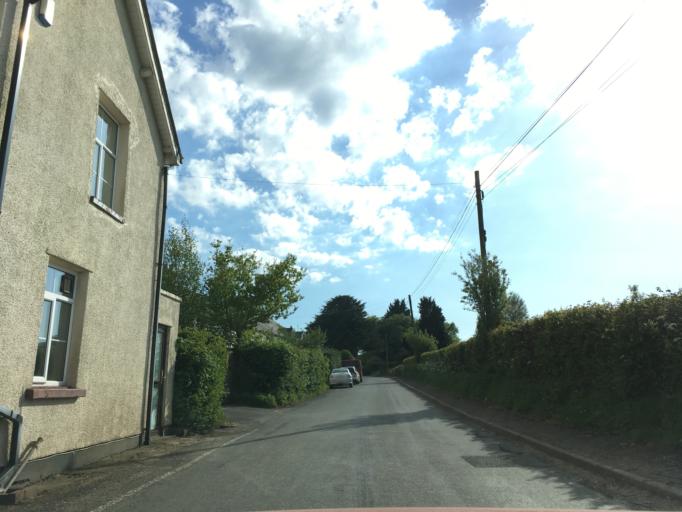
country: GB
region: Wales
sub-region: Newport
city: Marshfield
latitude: 51.5602
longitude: -3.0696
